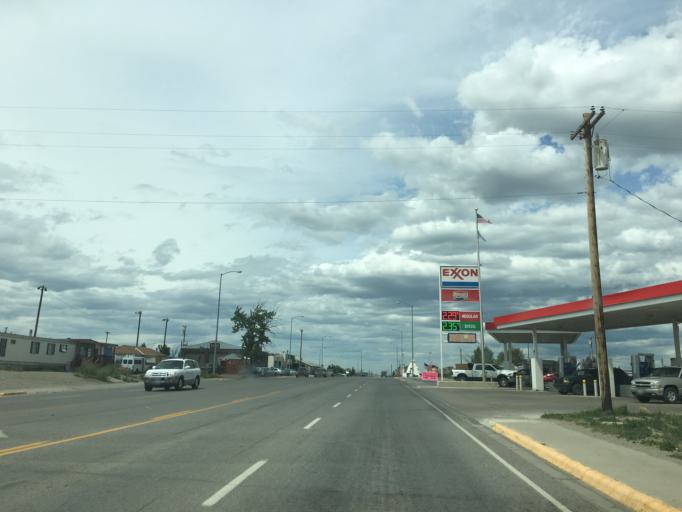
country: US
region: Montana
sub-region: Glacier County
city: Browning
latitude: 48.5531
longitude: -113.0098
